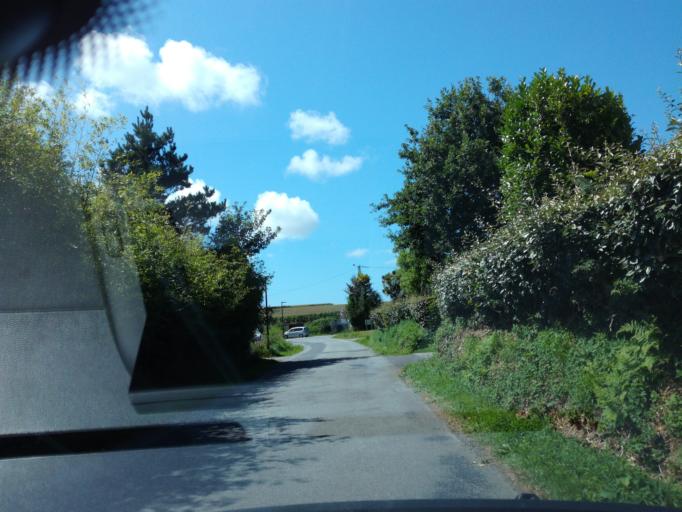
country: FR
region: Brittany
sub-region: Departement du Finistere
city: Saint-Pabu
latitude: 48.5622
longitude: -4.6000
